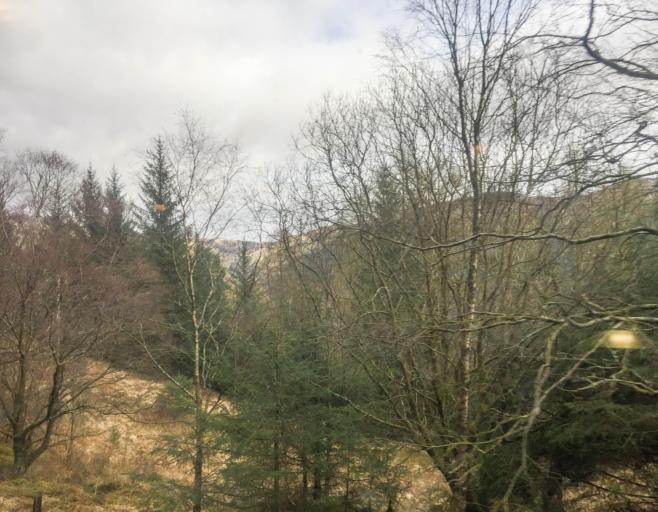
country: GB
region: Scotland
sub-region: Argyll and Bute
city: Garelochhead
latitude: 56.2123
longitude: -4.7020
